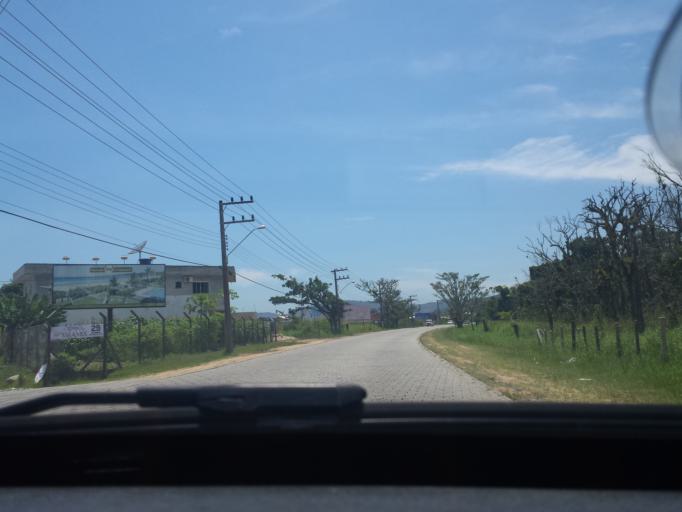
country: BR
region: Santa Catarina
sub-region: Porto Belo
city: Porto Belo
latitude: -27.1569
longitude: -48.5894
